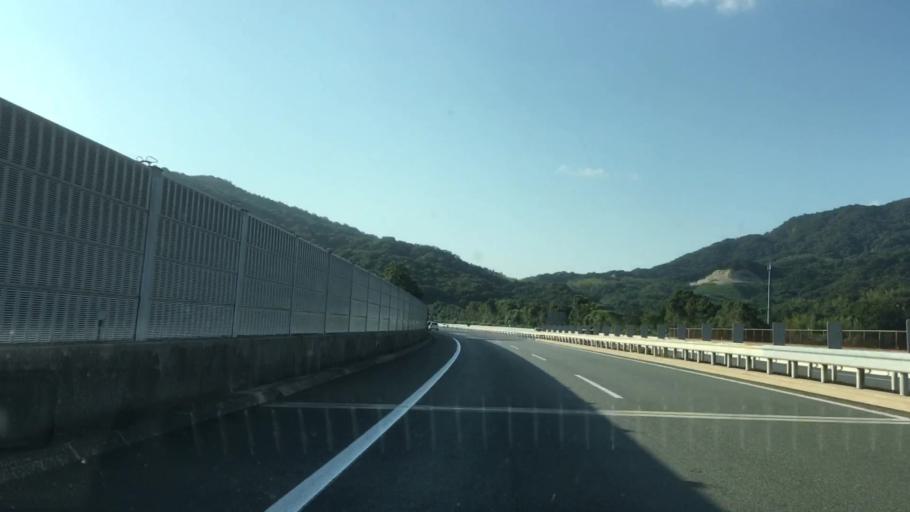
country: JP
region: Yamaguchi
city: Hofu
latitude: 34.0679
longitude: 131.6016
